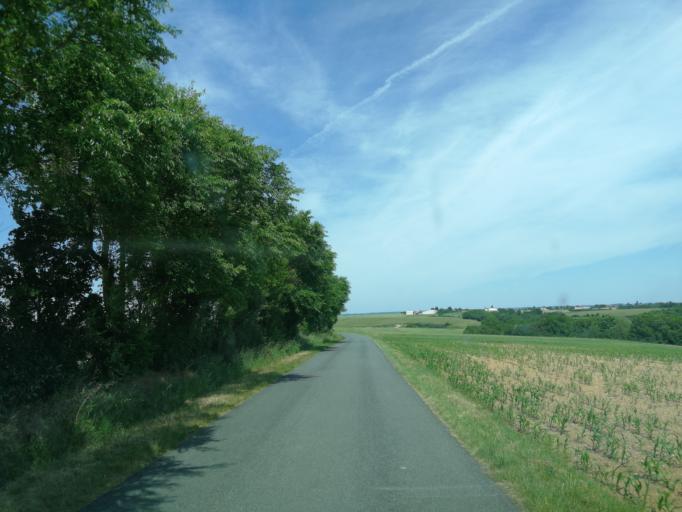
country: FR
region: Pays de la Loire
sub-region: Departement de la Vendee
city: Le Langon
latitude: 46.4308
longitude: -0.8901
